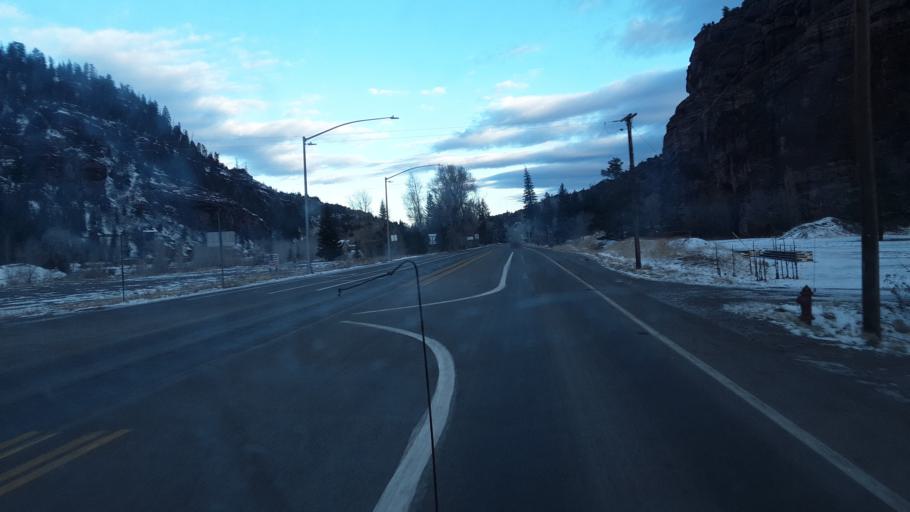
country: US
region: Colorado
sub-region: Ouray County
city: Ouray
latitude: 38.0396
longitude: -107.6793
